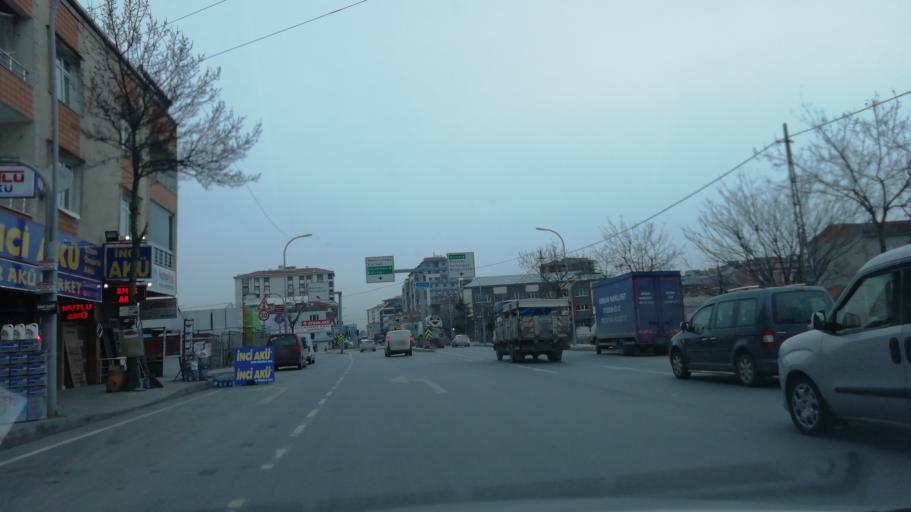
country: TR
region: Istanbul
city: Mahmutbey
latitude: 41.0472
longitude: 28.8302
